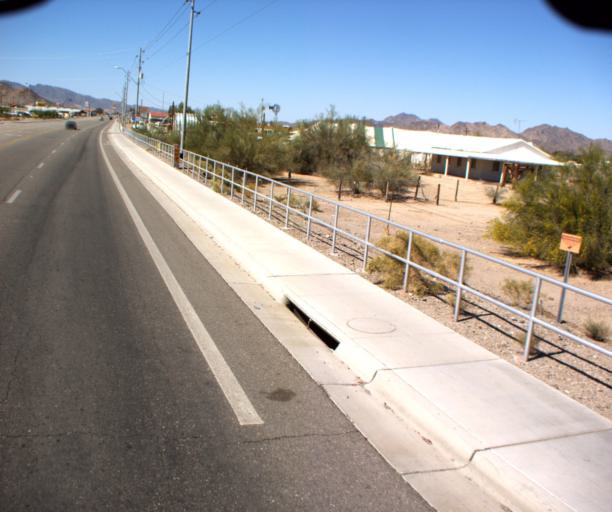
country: US
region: Arizona
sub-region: La Paz County
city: Quartzsite
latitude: 33.6645
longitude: -114.2287
